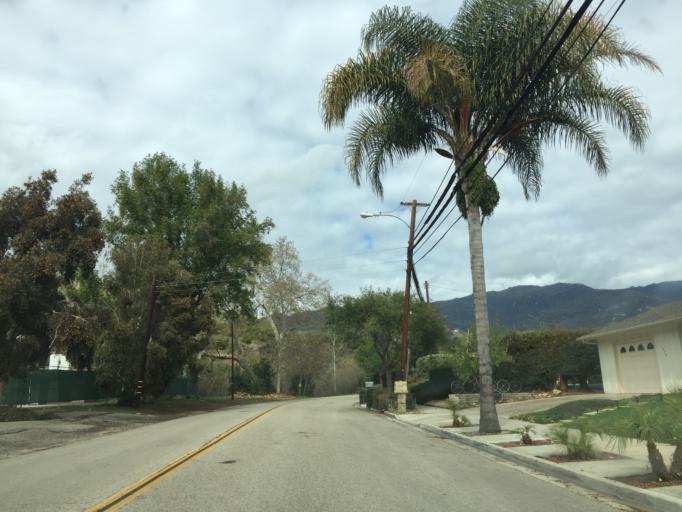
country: US
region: California
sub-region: Santa Barbara County
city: Goleta
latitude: 34.4564
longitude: -119.7961
